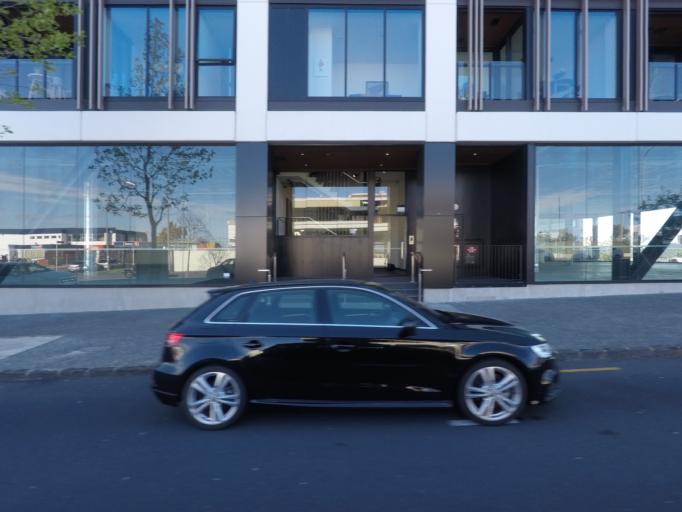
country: NZ
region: Auckland
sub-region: Auckland
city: Auckland
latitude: -36.8639
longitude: 174.7474
